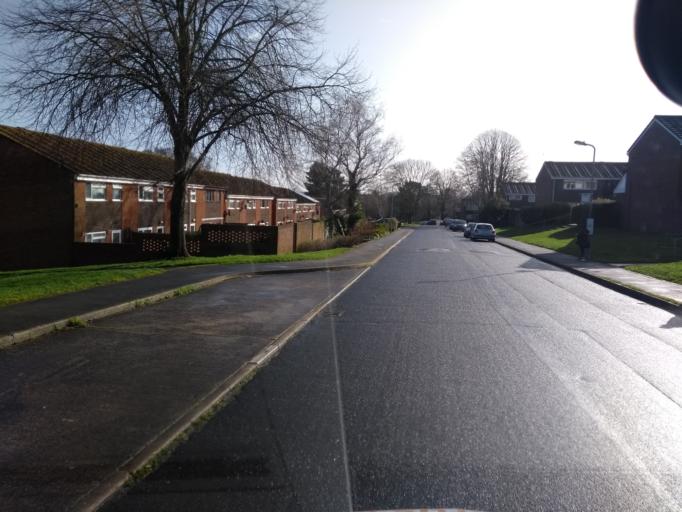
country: GB
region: England
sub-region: Somerset
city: Yeovil
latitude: 50.9534
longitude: -2.6123
